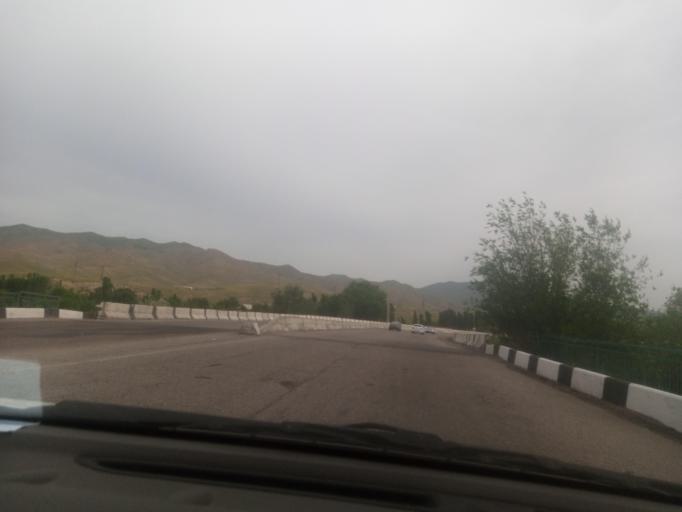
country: UZ
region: Toshkent
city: Angren
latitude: 40.9444
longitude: 69.9072
